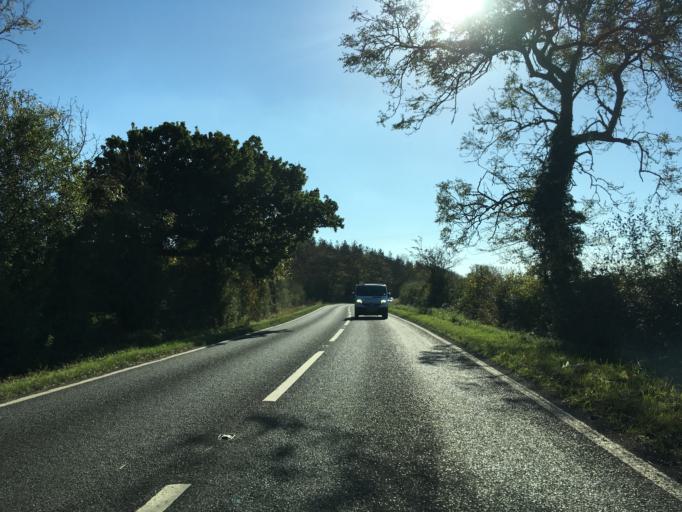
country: GB
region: England
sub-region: South Gloucestershire
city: Wickwar
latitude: 51.5682
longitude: -2.3976
